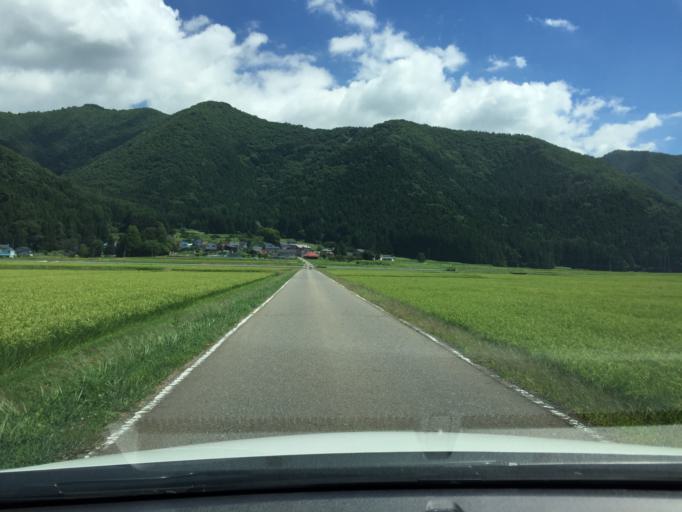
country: JP
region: Fukushima
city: Inawashiro
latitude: 37.5725
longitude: 140.1320
